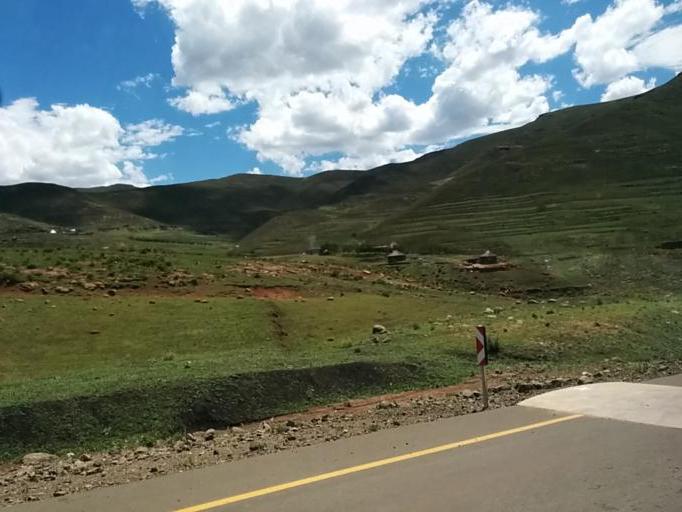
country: LS
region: Maseru
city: Nako
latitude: -29.9560
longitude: 28.1501
